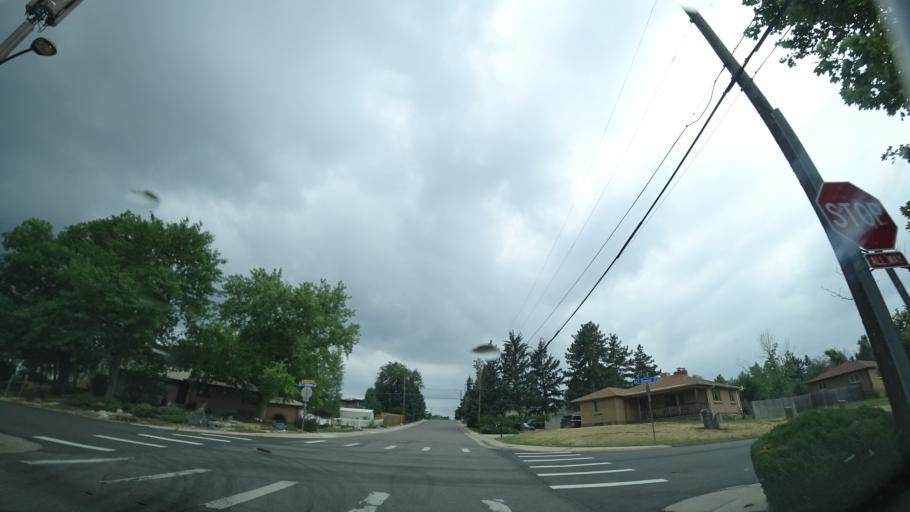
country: US
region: Colorado
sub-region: Jefferson County
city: Lakewood
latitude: 39.7062
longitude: -105.1238
